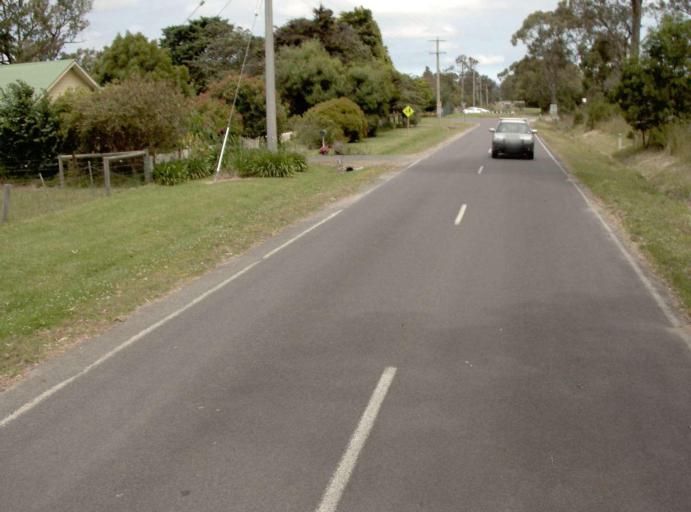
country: AU
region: Victoria
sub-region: Latrobe
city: Traralgon
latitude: -38.5173
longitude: 146.6479
